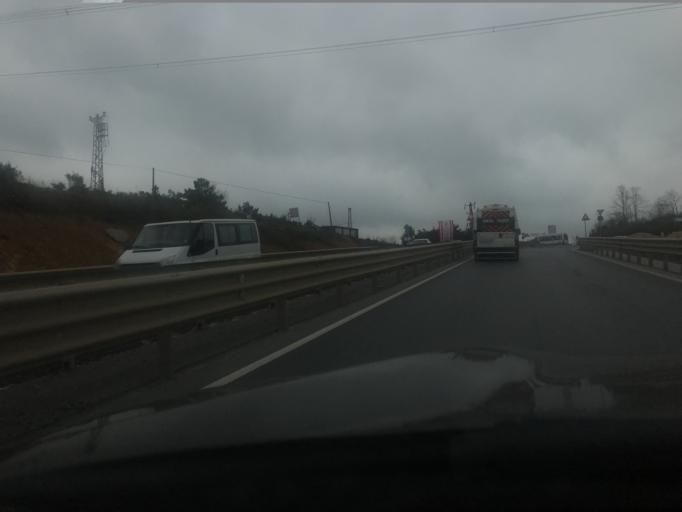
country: TR
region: Istanbul
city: Umraniye
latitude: 41.0553
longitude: 29.1687
